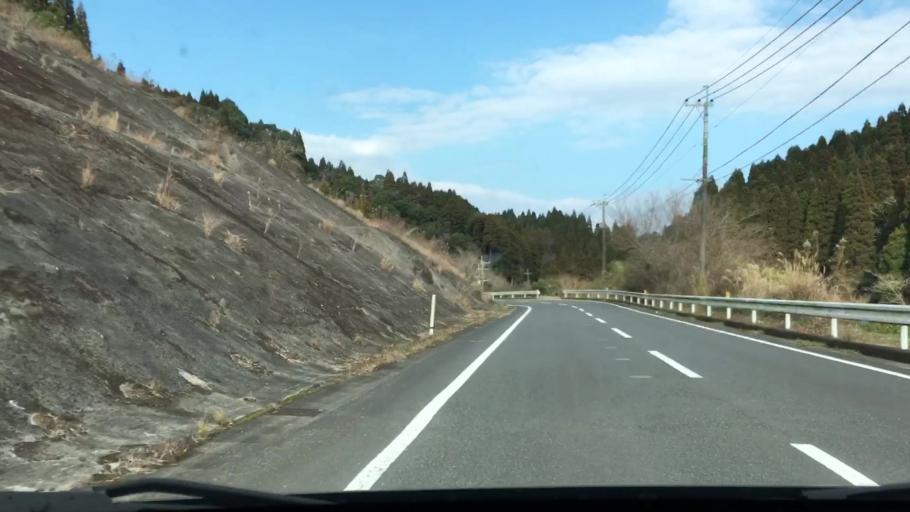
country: JP
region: Miyazaki
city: Kushima
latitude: 31.5692
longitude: 131.2611
